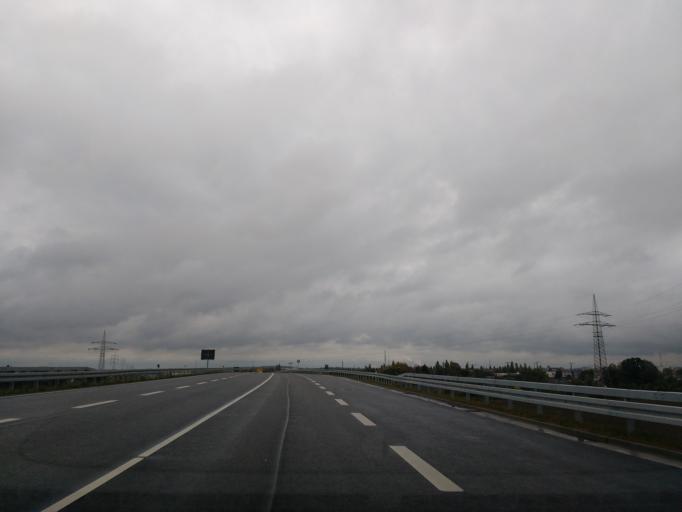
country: DE
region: Saxony-Anhalt
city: Halle (Saale)
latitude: 51.5008
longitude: 12.0160
